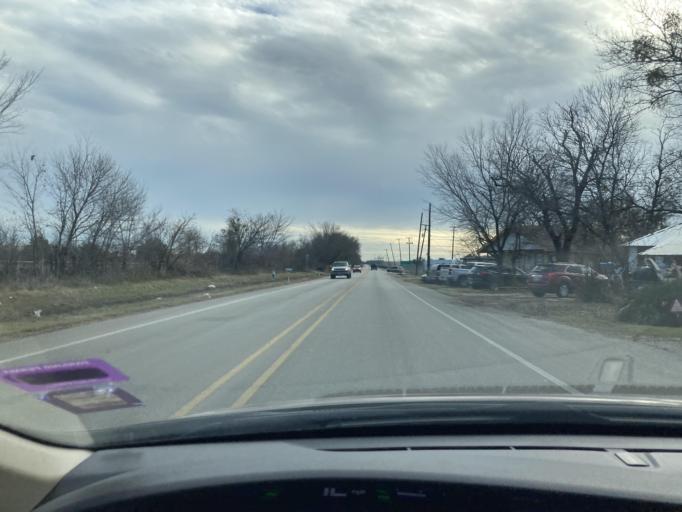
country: US
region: Texas
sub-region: Navarro County
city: Corsicana
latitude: 32.0800
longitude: -96.4608
